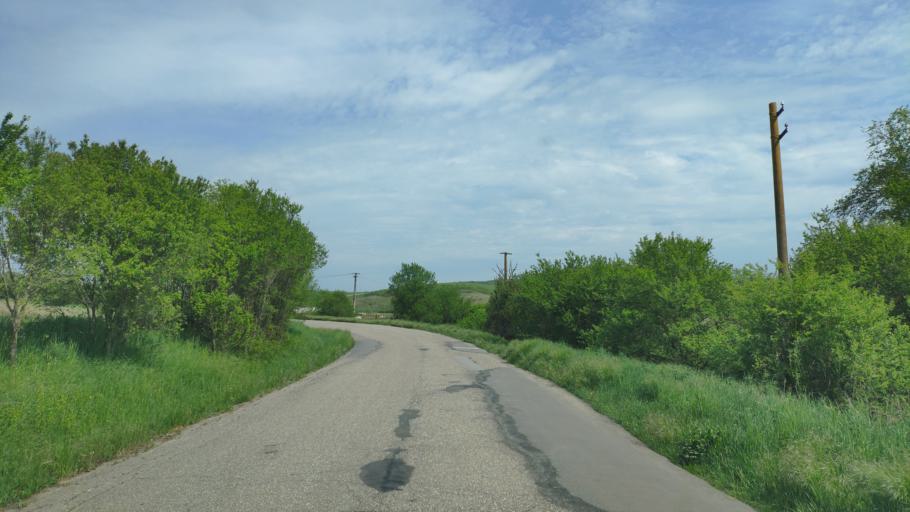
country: HU
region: Borsod-Abauj-Zemplen
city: Ozd
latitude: 48.4123
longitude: 20.2374
